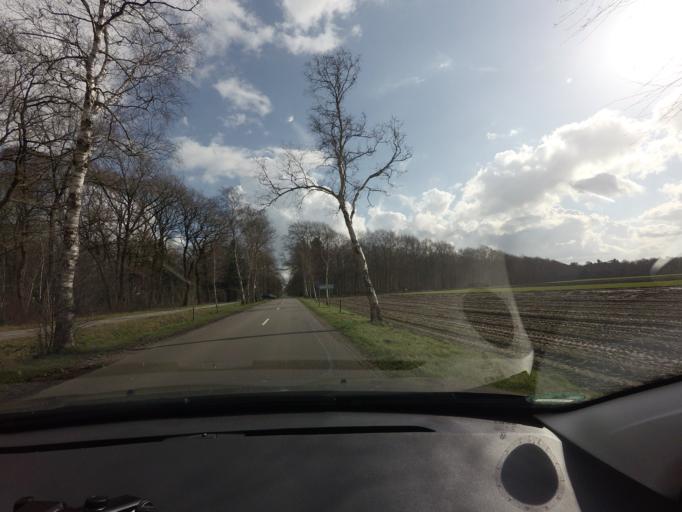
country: NL
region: Drenthe
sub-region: Gemeente Assen
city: Assen
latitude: 52.9050
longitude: 6.5466
